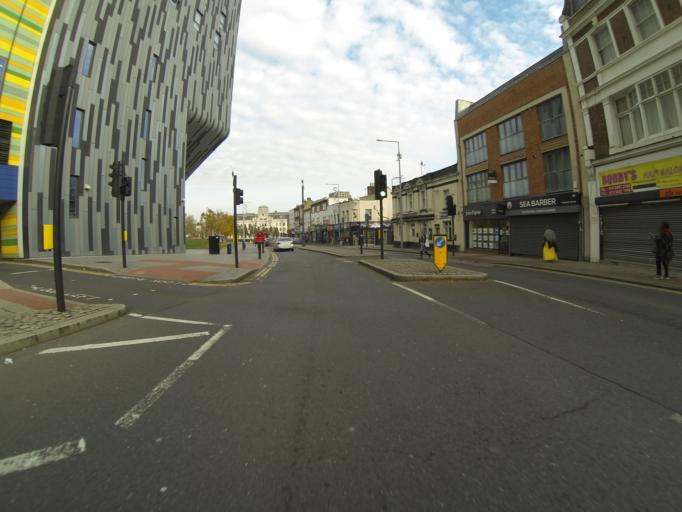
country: GB
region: England
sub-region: Greater London
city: Woolwich
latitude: 51.4885
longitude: 0.0661
